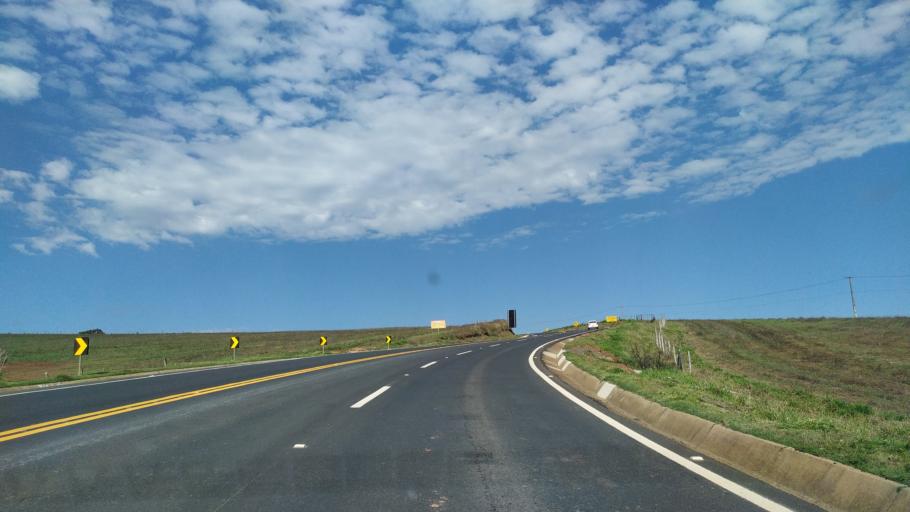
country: BR
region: Parana
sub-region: Telemaco Borba
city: Telemaco Borba
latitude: -24.2782
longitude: -50.7135
